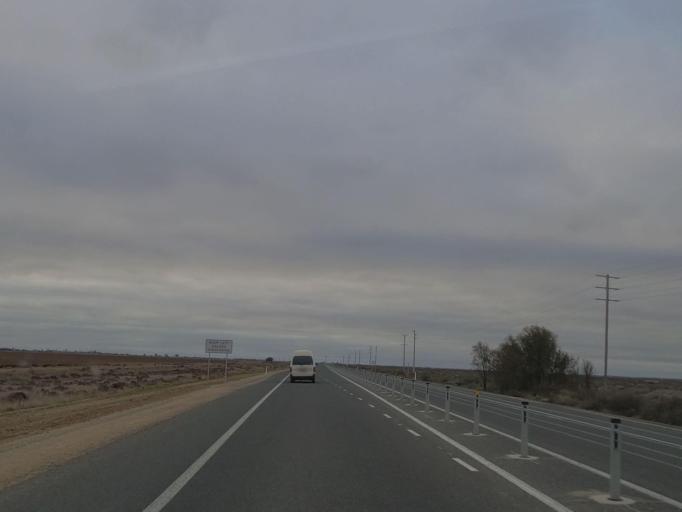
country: AU
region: Victoria
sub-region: Swan Hill
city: Swan Hill
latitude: -35.5165
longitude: 143.7284
